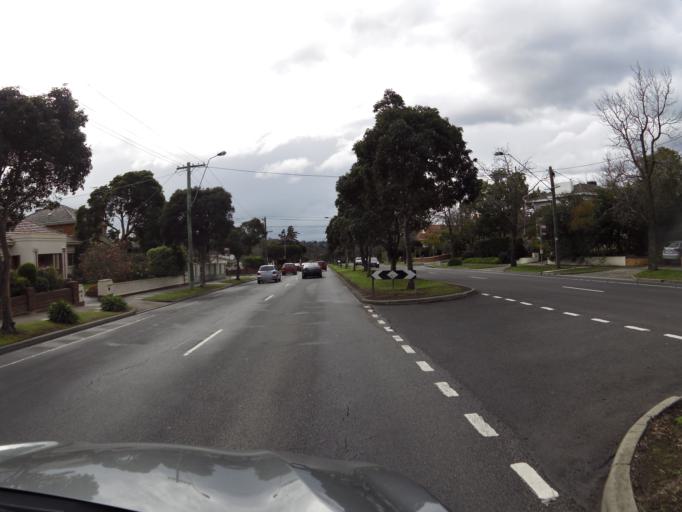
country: AU
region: Victoria
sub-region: Boroondara
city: Kew East
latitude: -37.7909
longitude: 145.0644
